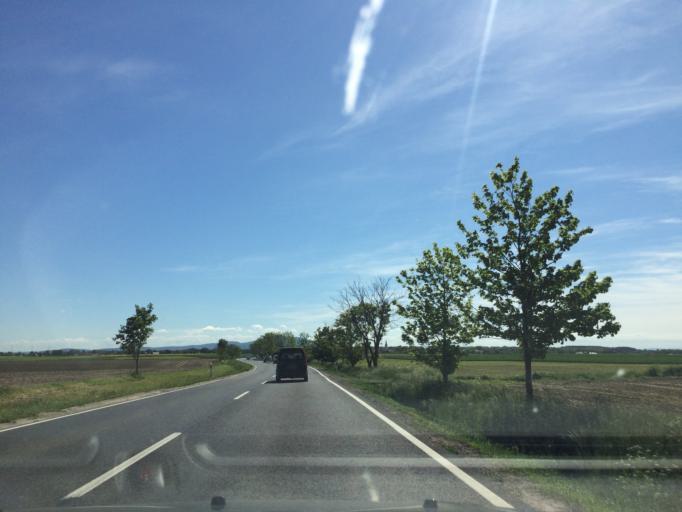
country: PL
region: Lower Silesian Voivodeship
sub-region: Powiat wroclawski
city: Gniechowice
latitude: 50.9995
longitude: 16.8499
